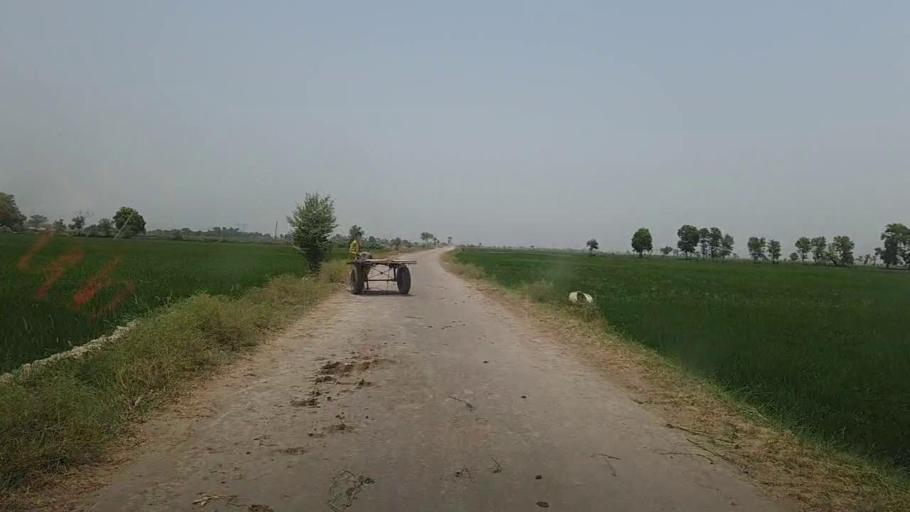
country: PK
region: Sindh
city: Sita Road
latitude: 27.0547
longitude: 67.8482
